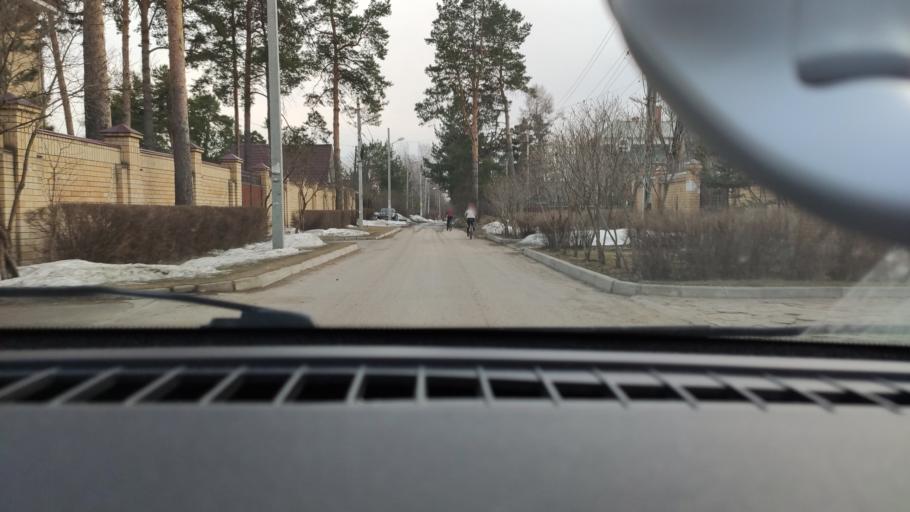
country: RU
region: Perm
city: Perm
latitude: 58.0538
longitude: 56.3000
